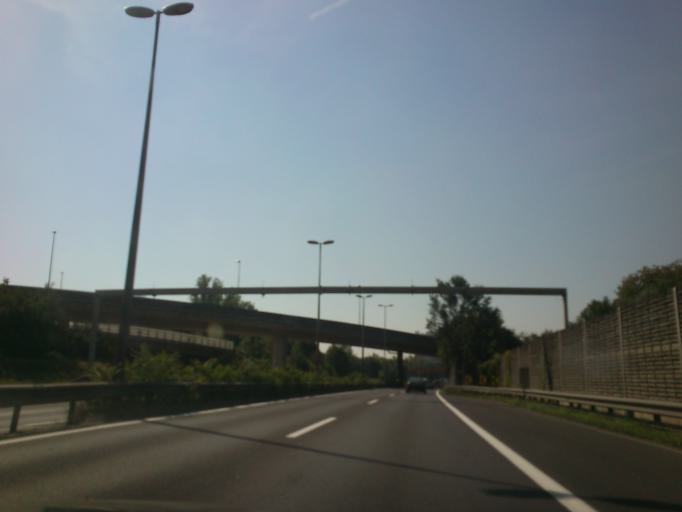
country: AT
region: Upper Austria
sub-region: Linz Stadt
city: Linz
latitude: 48.2964
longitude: 14.3177
